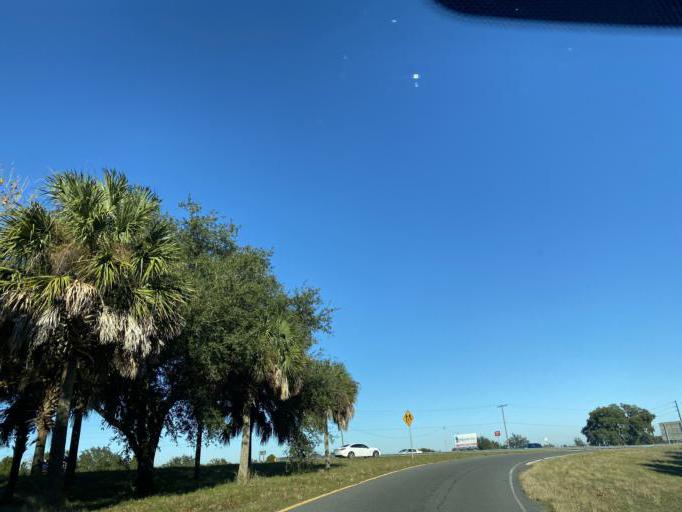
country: US
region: Florida
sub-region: Lake County
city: Howie In The Hills
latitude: 28.6423
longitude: -81.8088
